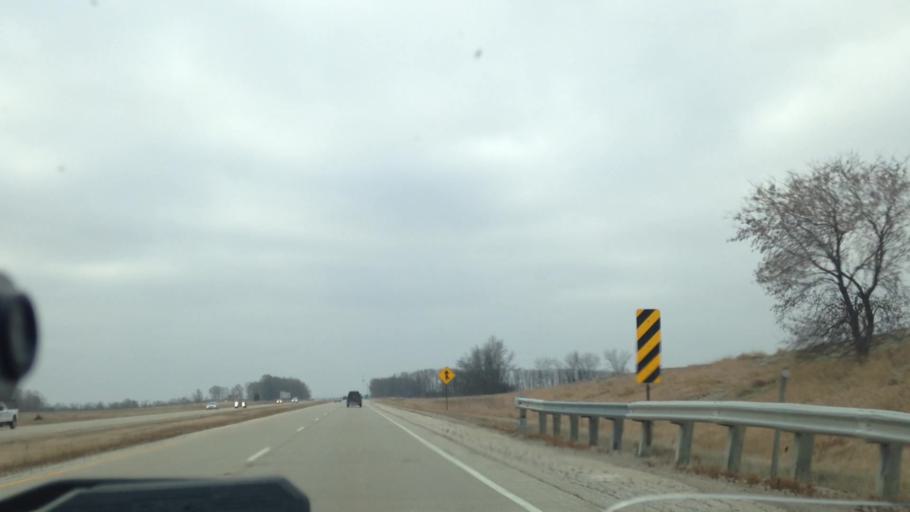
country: US
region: Wisconsin
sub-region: Washington County
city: Jackson
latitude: 43.3532
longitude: -88.1911
